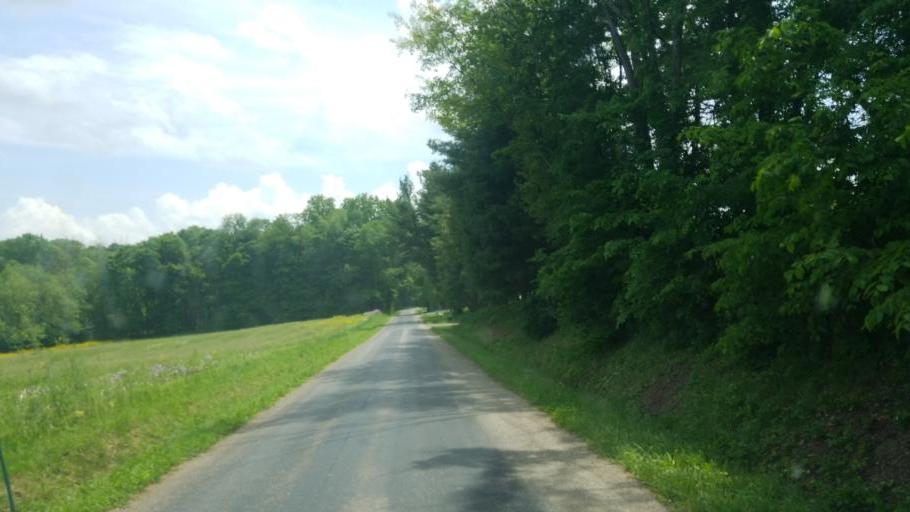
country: US
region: Ohio
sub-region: Ashland County
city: Ashland
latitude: 40.7719
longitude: -82.3396
